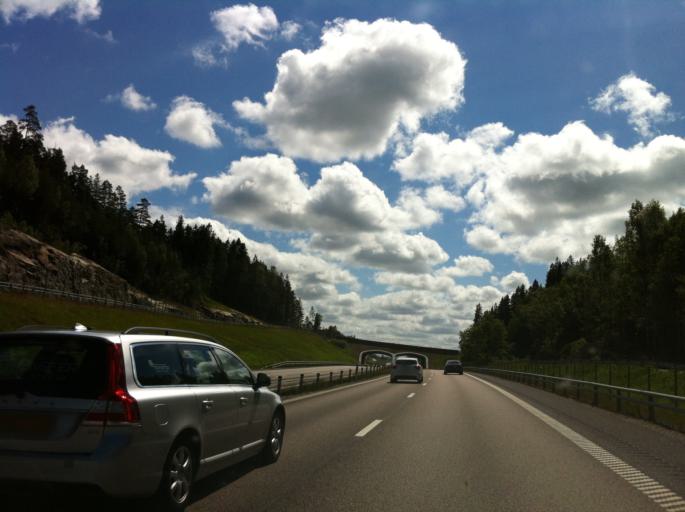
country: SE
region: Vaestra Goetaland
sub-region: Lilla Edets Kommun
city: Lilla Edet
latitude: 58.1842
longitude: 12.1423
